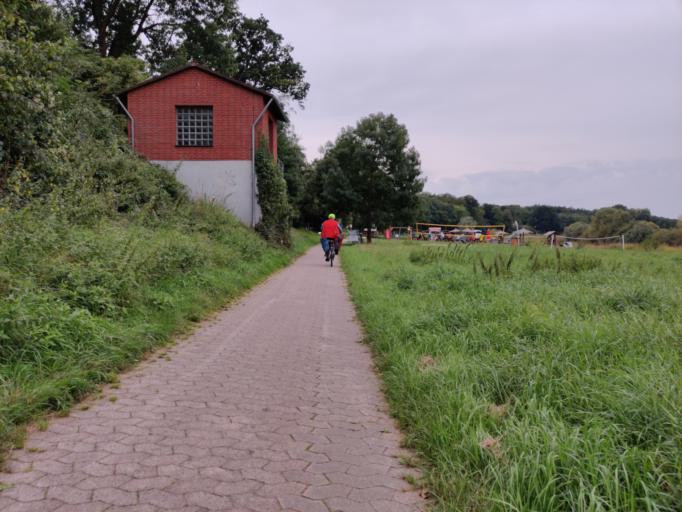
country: DE
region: Lower Saxony
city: Heinsen
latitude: 51.9013
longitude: 9.4677
